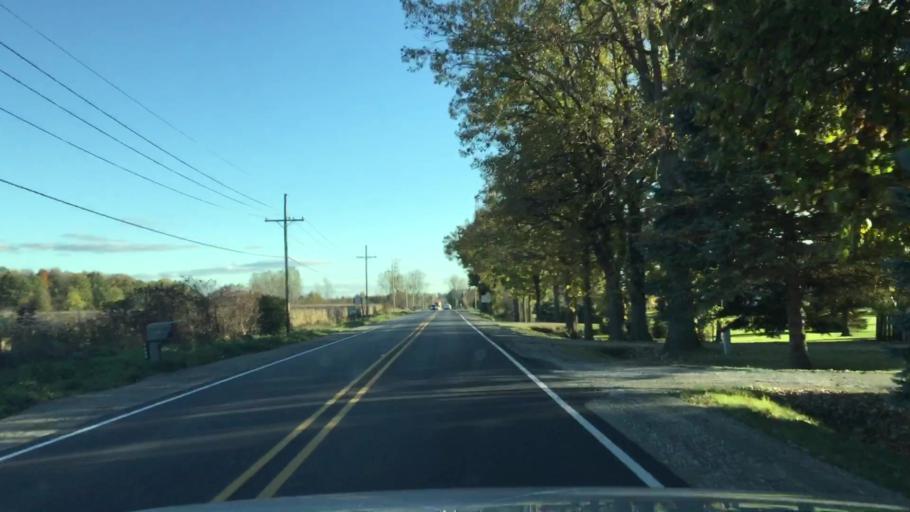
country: US
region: Michigan
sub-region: Lapeer County
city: Almont
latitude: 42.9441
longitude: -83.1448
